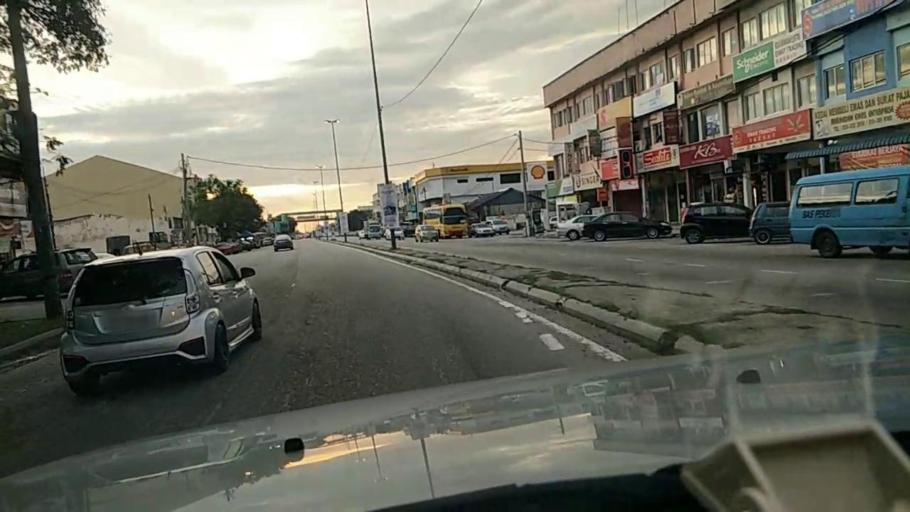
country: MY
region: Perak
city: Kampong Dungun
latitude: 3.1368
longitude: 101.3754
